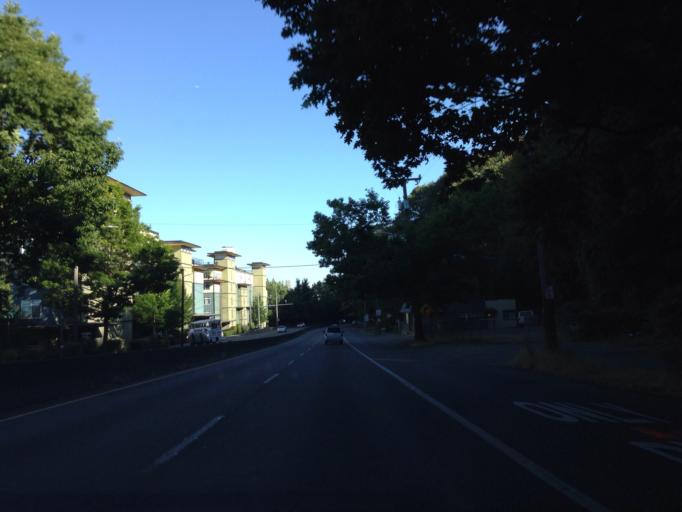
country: US
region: Washington
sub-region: King County
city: Seattle
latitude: 47.6378
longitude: -122.3448
